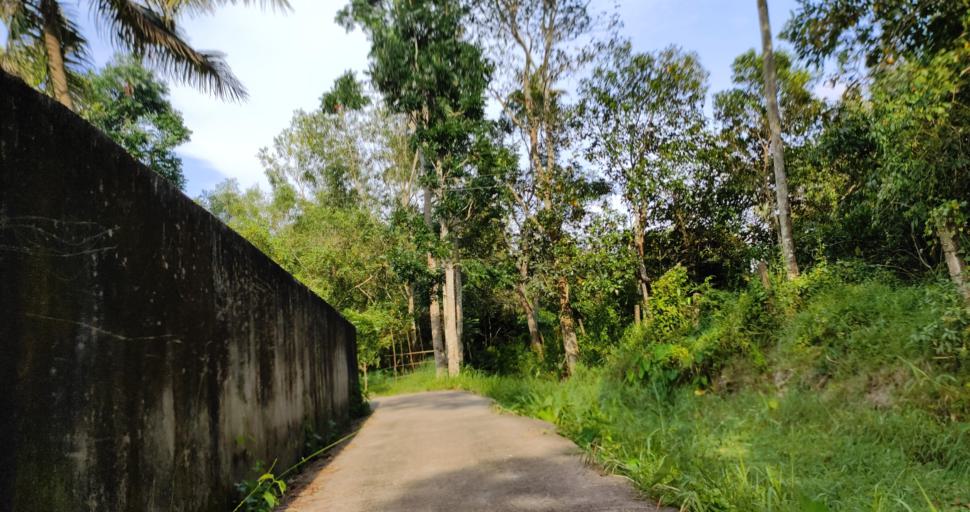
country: IN
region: Kerala
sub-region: Alappuzha
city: Shertallai
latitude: 9.6045
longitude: 76.3302
